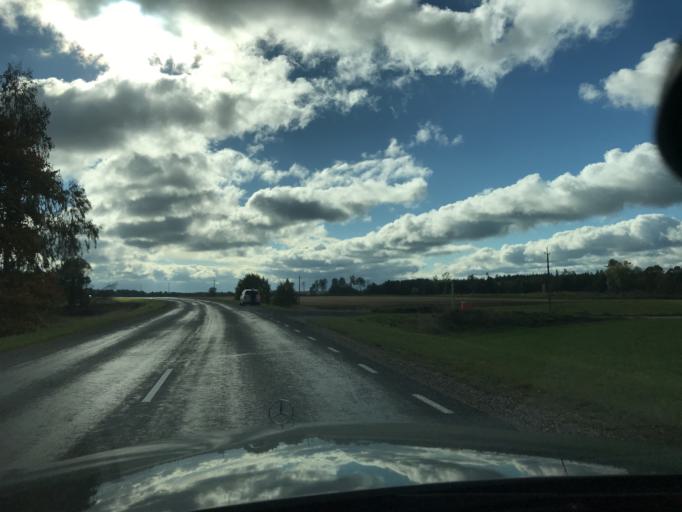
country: EE
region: Valgamaa
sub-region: Valga linn
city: Valga
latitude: 57.9725
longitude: 26.2605
